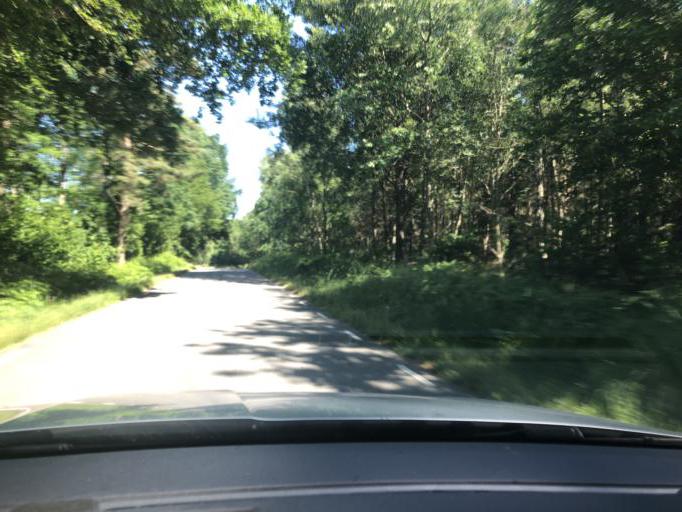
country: SE
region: Blekinge
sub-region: Karlshamns Kommun
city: Morrum
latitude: 56.1716
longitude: 14.6501
